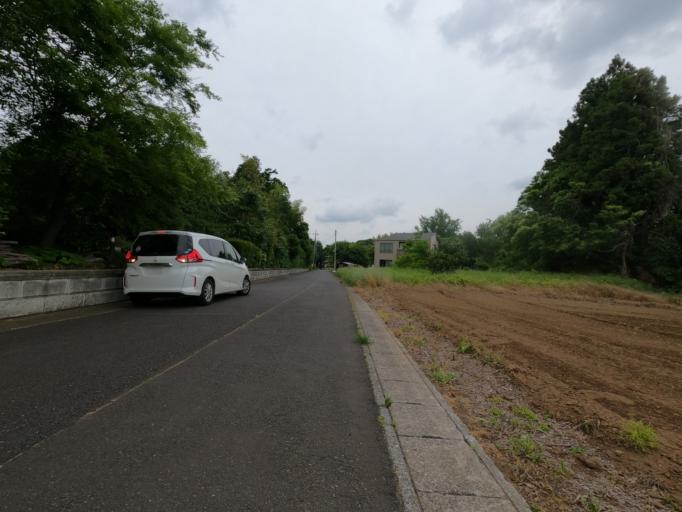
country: JP
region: Ibaraki
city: Moriya
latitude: 35.9526
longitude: 139.9684
